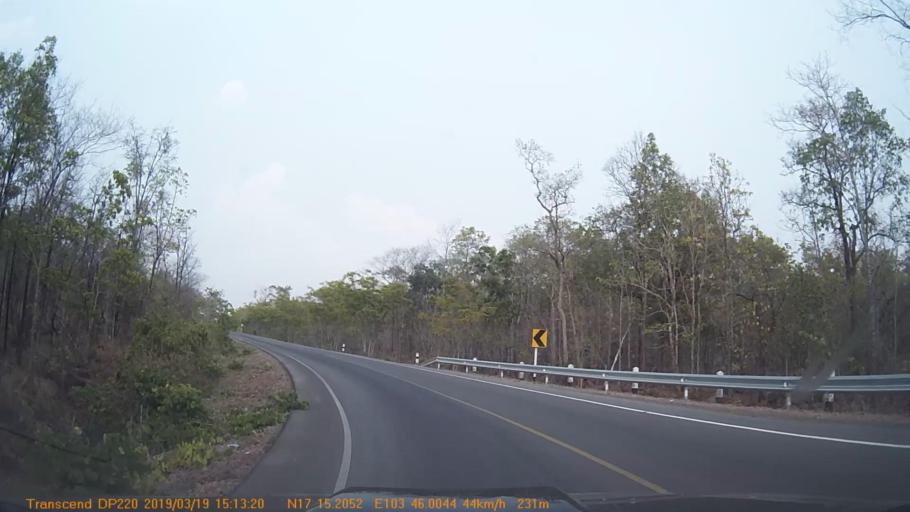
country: TH
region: Sakon Nakhon
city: Nikhom Nam Un
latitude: 17.2534
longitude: 103.7670
